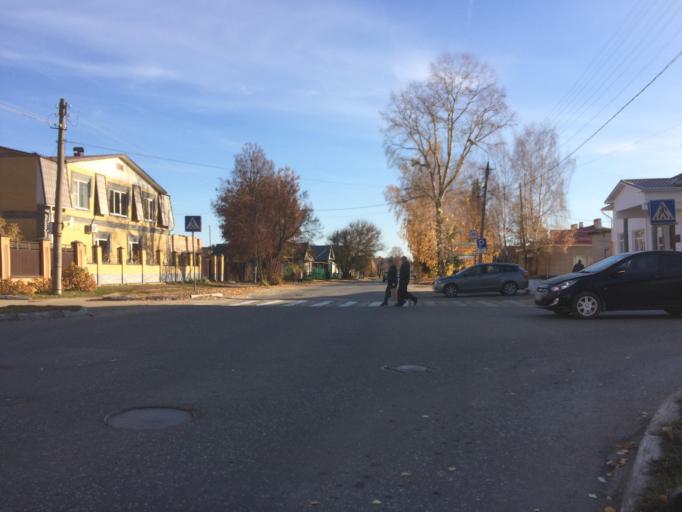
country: RU
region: Mariy-El
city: Medvedevo
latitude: 56.6335
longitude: 47.8081
